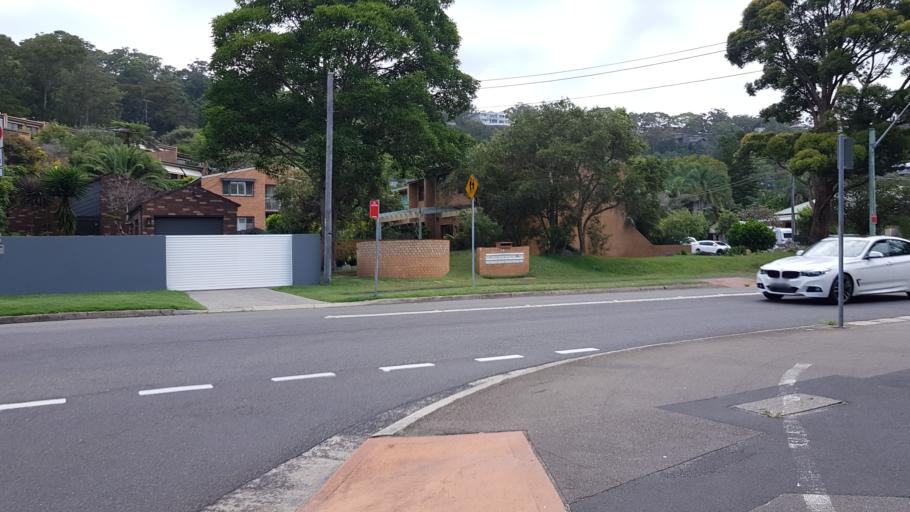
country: AU
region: New South Wales
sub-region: Warringah
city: Narrabeen
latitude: -33.7215
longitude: 151.2943
